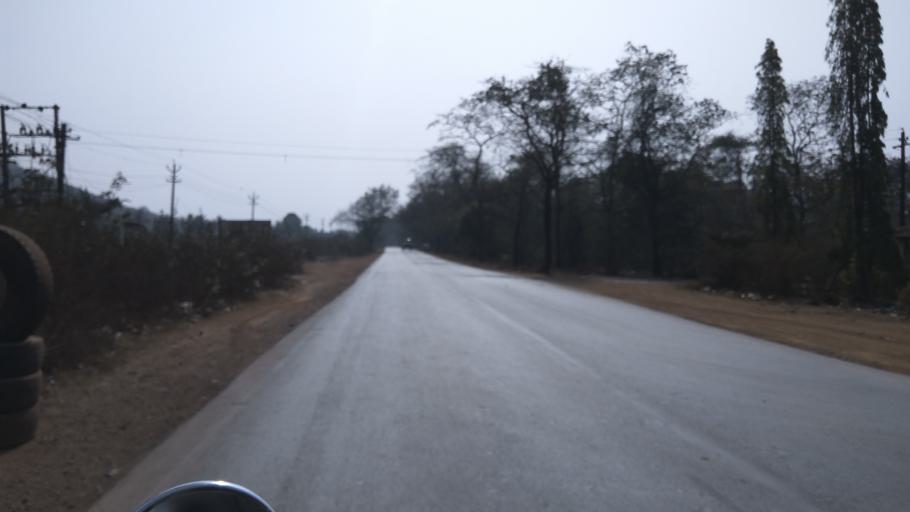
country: IN
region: Goa
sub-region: North Goa
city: Palle
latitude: 15.4031
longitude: 74.0967
